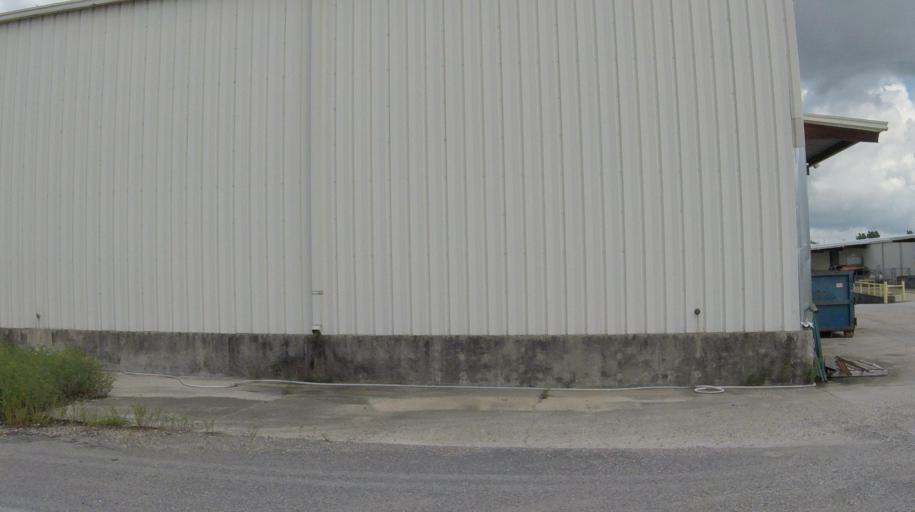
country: US
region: Louisiana
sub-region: West Baton Rouge Parish
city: Port Allen
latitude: 30.4665
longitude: -91.1872
